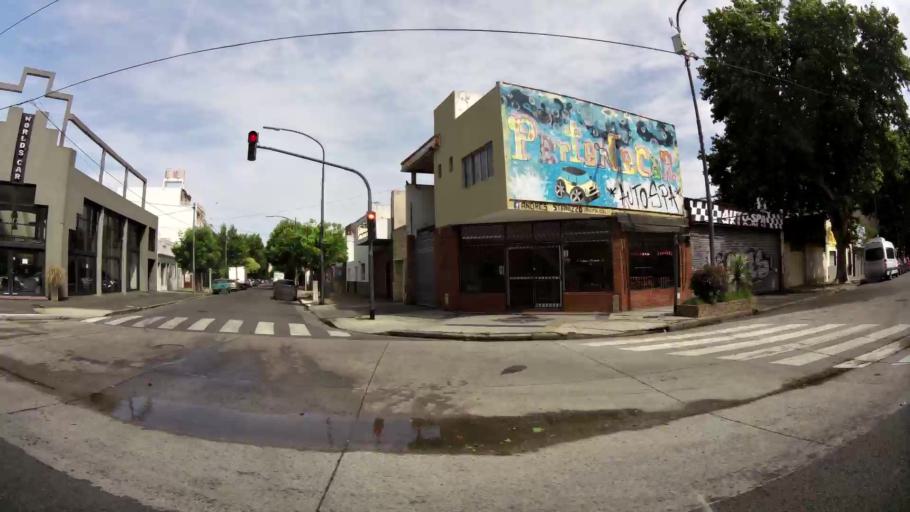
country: AR
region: Buenos Aires F.D.
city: Villa Lugano
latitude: -34.6498
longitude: -58.5106
